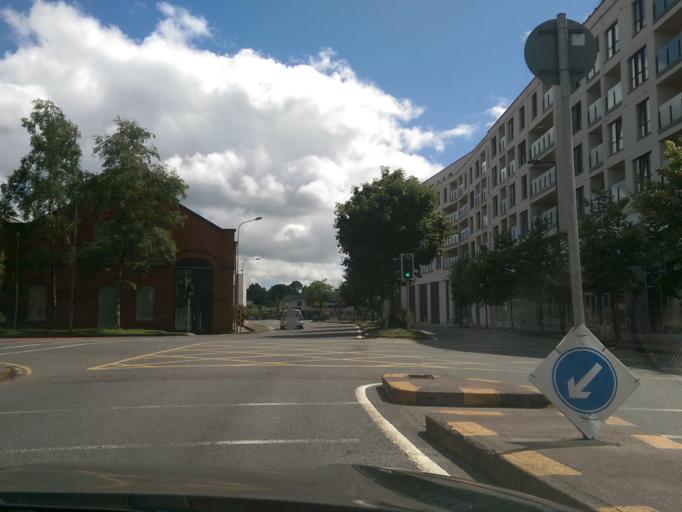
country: IE
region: Munster
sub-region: County Cork
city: Cork
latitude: 51.8975
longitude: -8.4629
